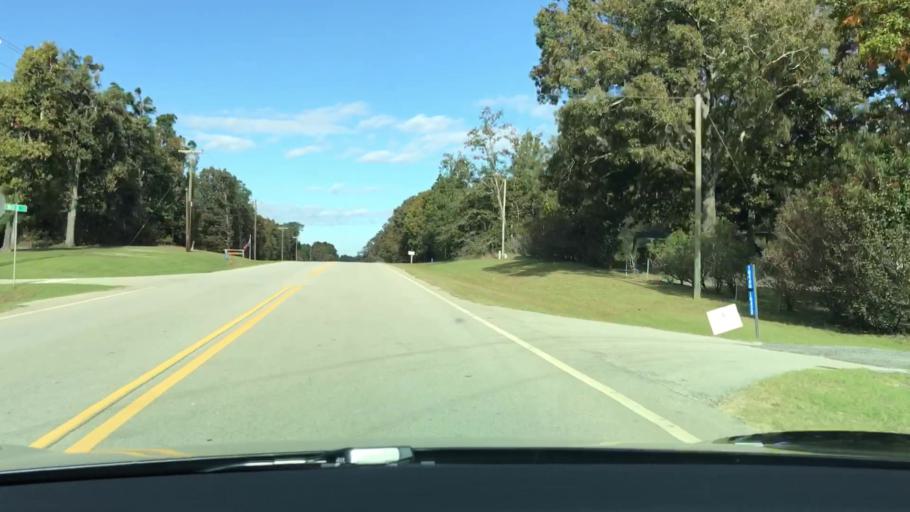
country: US
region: Georgia
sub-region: Jefferson County
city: Wrens
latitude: 33.1897
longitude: -82.4570
